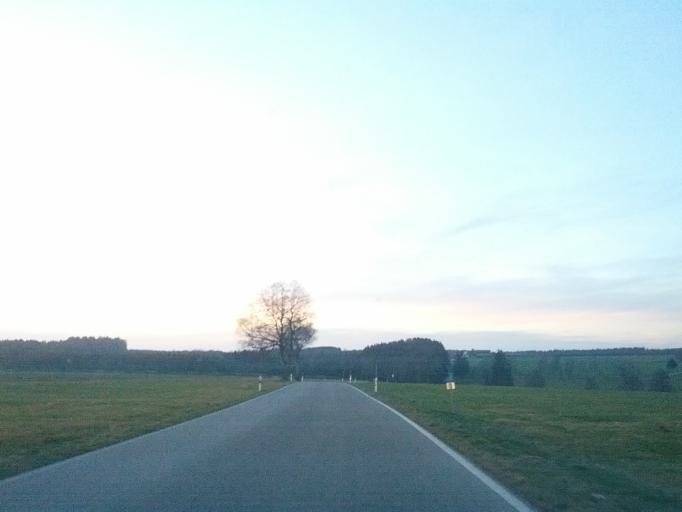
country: DE
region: Baden-Wuerttemberg
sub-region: Tuebingen Region
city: Aitrach
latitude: 47.9398
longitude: 10.0194
